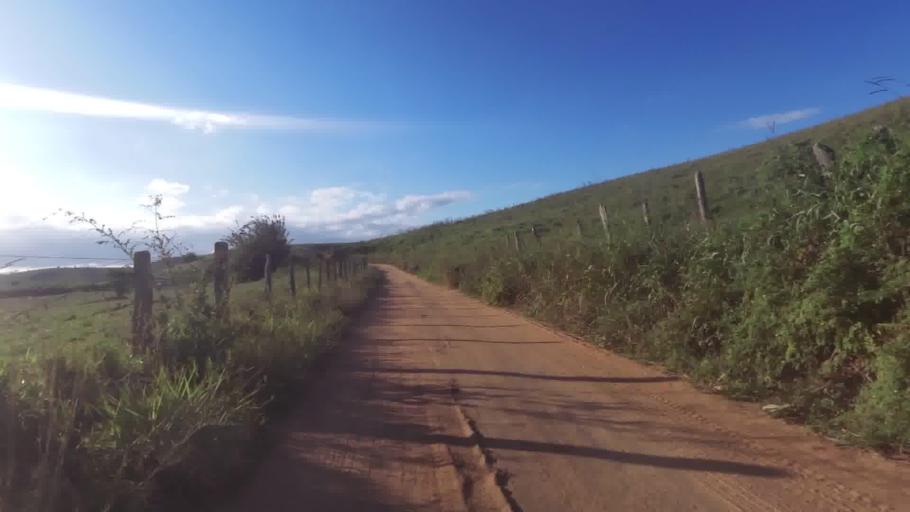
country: BR
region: Espirito Santo
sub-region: Marataizes
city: Marataizes
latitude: -21.1356
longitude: -41.0180
